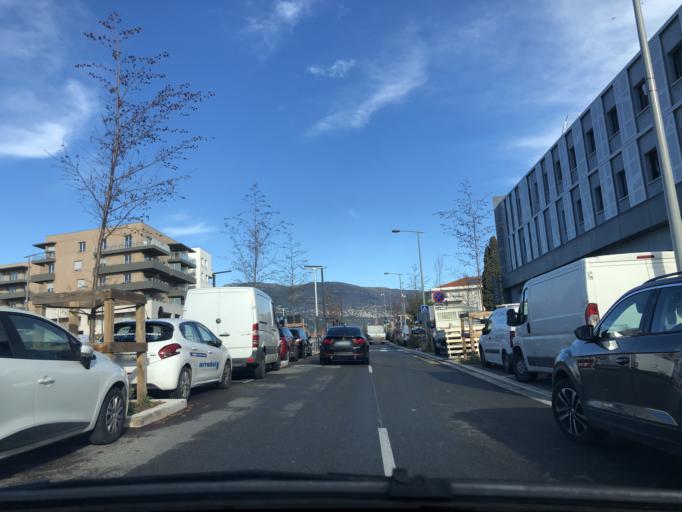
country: FR
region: Provence-Alpes-Cote d'Azur
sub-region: Departement des Alpes-Maritimes
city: Saint-Laurent-du-Var
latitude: 43.7098
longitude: 7.1952
